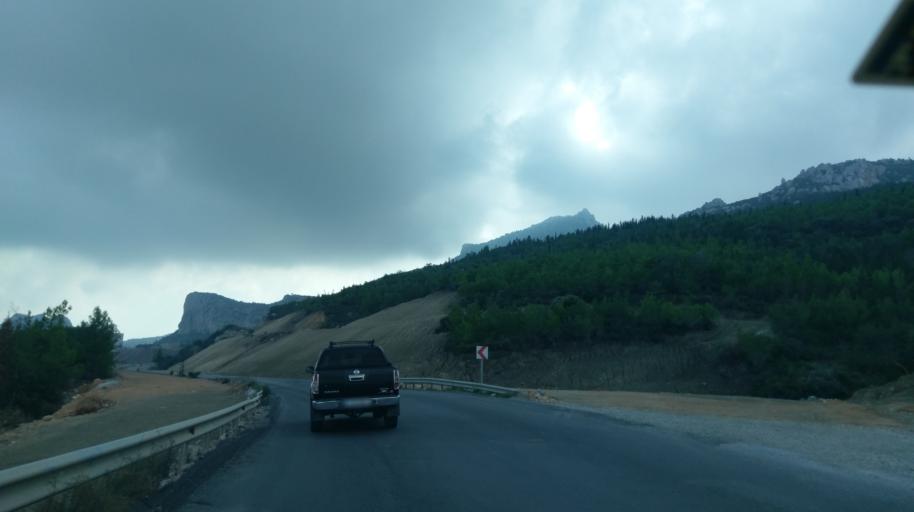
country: CY
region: Keryneia
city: Kyrenia
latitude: 35.2964
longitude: 33.4383
